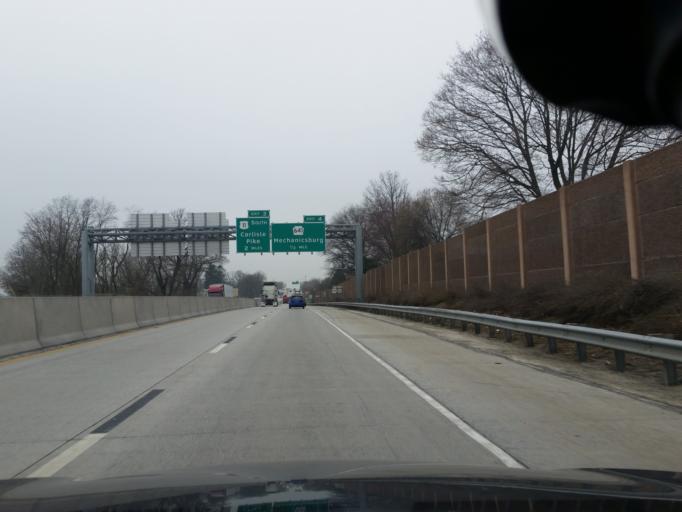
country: US
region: Pennsylvania
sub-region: Cumberland County
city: Shiremanstown
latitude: 40.2321
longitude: -76.9405
